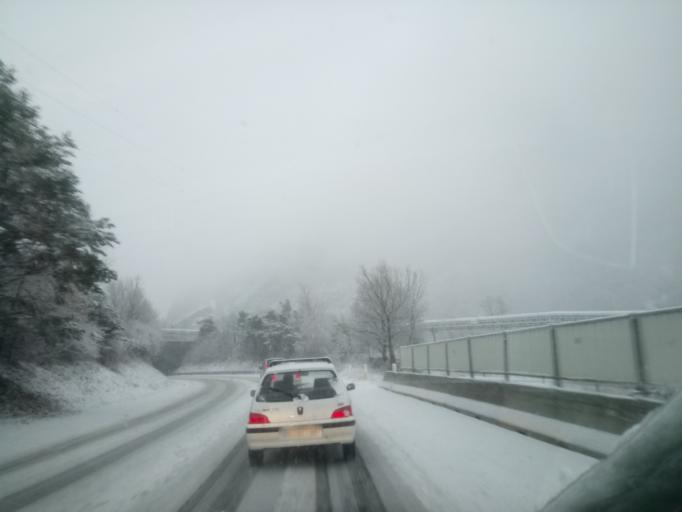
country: FR
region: Rhone-Alpes
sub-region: Departement de la Savoie
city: Saint-Michel-de-Maurienne
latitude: 45.2376
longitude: 6.4369
